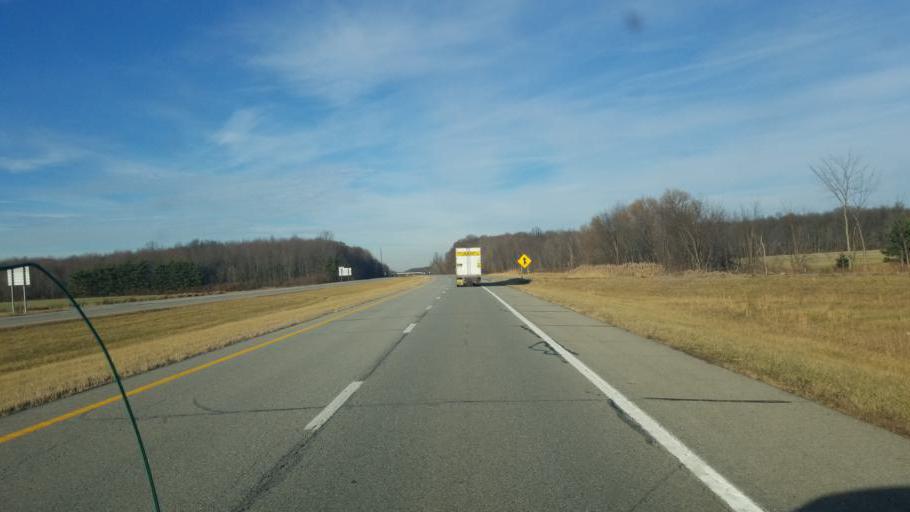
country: US
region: Ohio
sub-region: Trumbull County
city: Cortland
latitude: 41.4642
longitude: -80.7122
